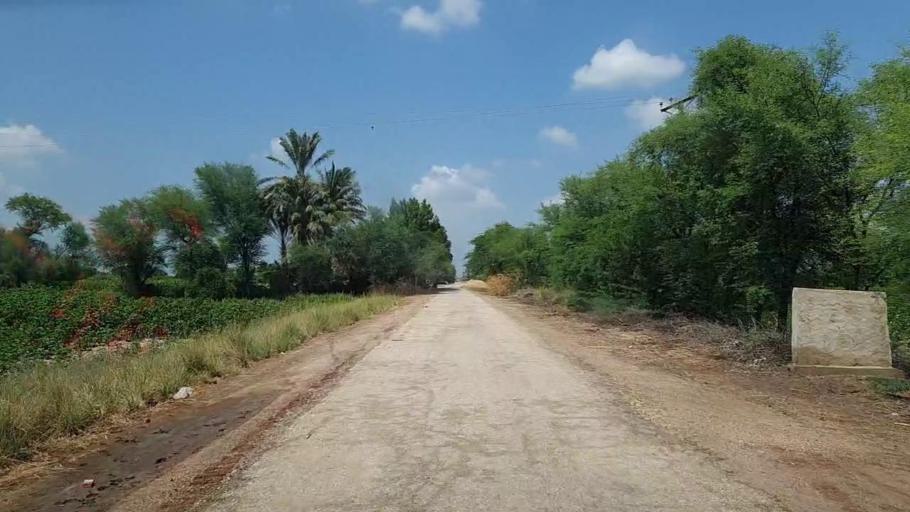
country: PK
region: Sindh
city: Kandiaro
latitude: 27.0218
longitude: 68.2716
